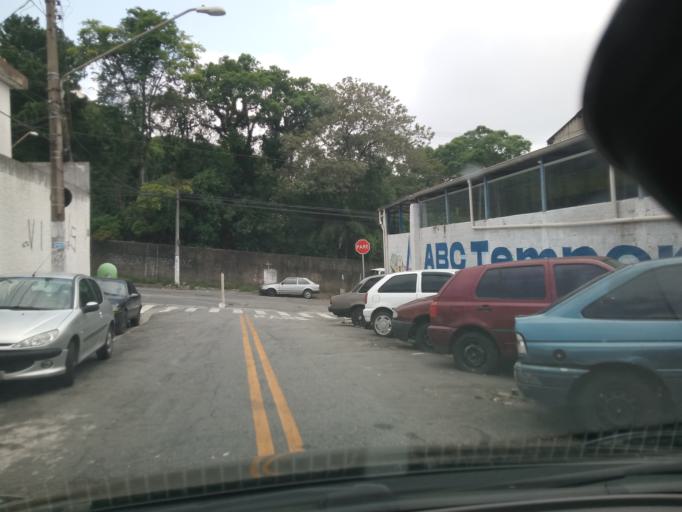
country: BR
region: Sao Paulo
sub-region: Sao Bernardo Do Campo
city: Sao Bernardo do Campo
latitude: -23.7049
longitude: -46.5701
